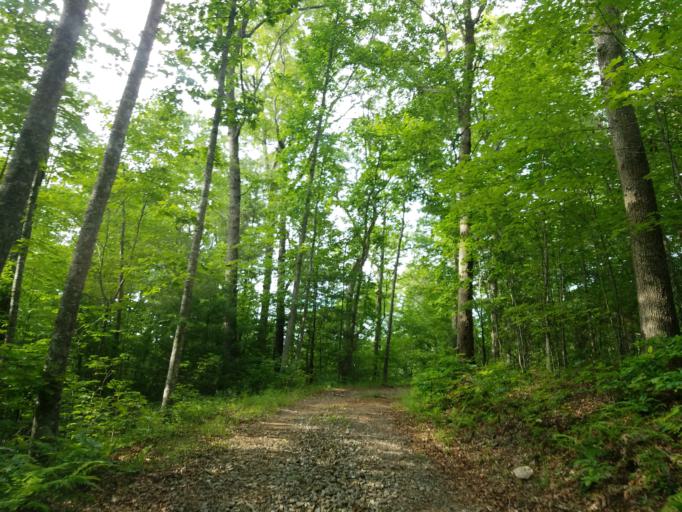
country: US
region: Georgia
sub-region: Fannin County
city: Blue Ridge
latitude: 34.7249
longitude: -84.1946
